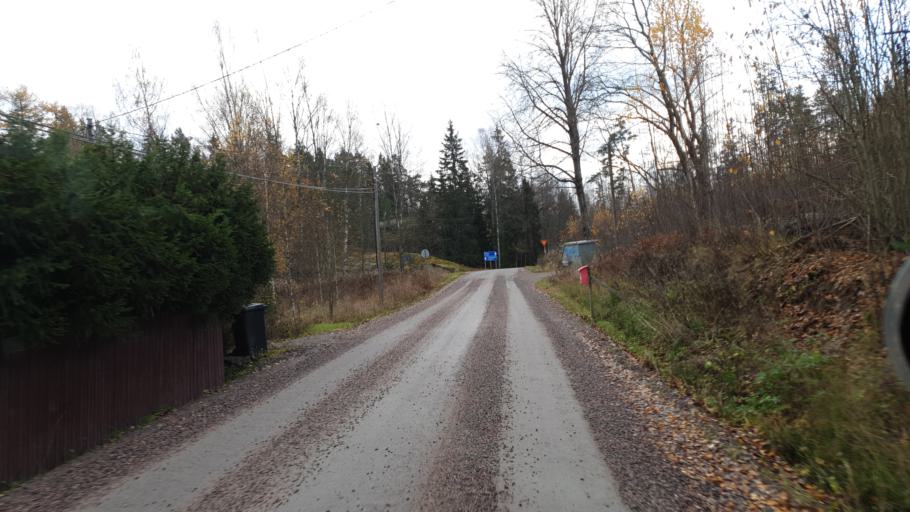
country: FI
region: Uusimaa
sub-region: Helsinki
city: Siuntio
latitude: 60.1151
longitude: 24.3007
